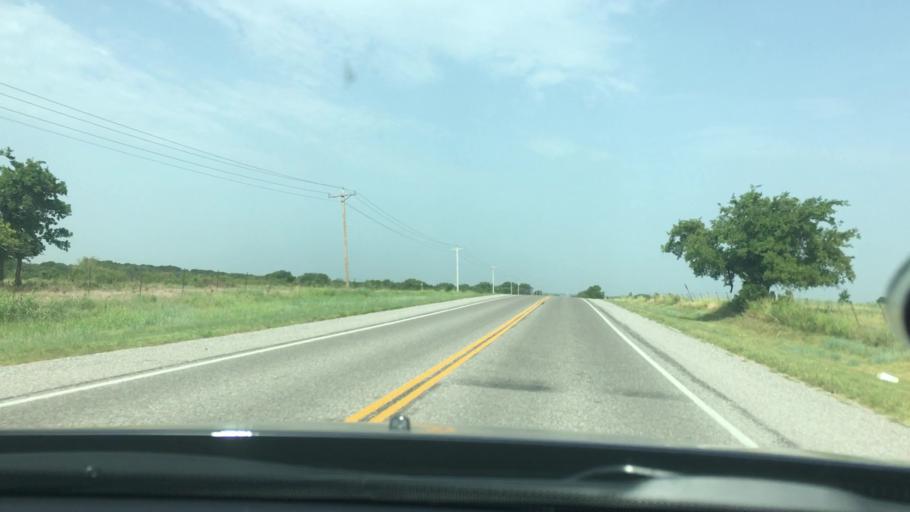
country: US
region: Oklahoma
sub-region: Garvin County
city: Stratford
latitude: 34.7966
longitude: -97.0926
